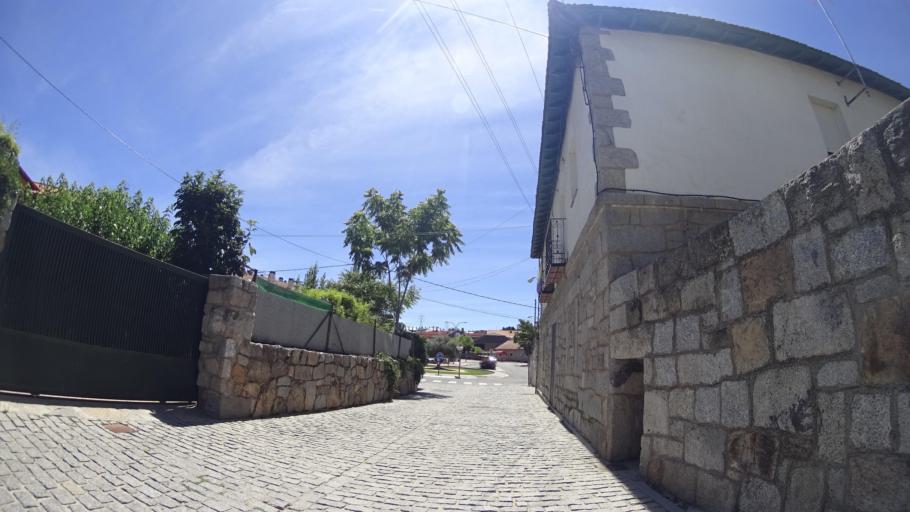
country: ES
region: Madrid
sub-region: Provincia de Madrid
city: Collado-Villalba
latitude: 40.6458
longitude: -3.9911
